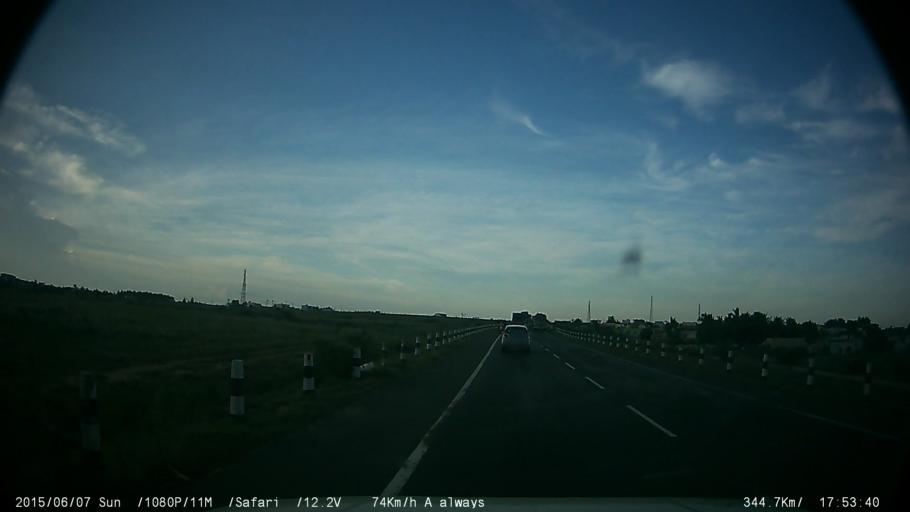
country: IN
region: Tamil Nadu
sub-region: Coimbatore
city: Chettipalaiyam
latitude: 10.9386
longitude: 77.0057
